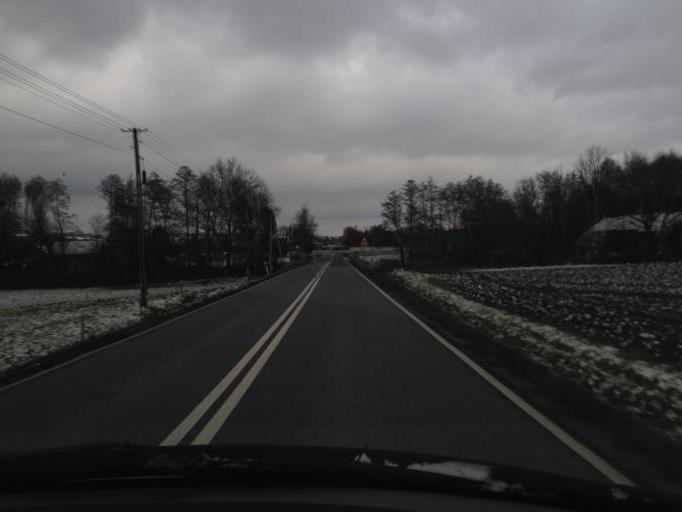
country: PL
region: Lesser Poland Voivodeship
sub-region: Powiat tarnowski
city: Janowice
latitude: 49.8552
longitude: 20.8666
